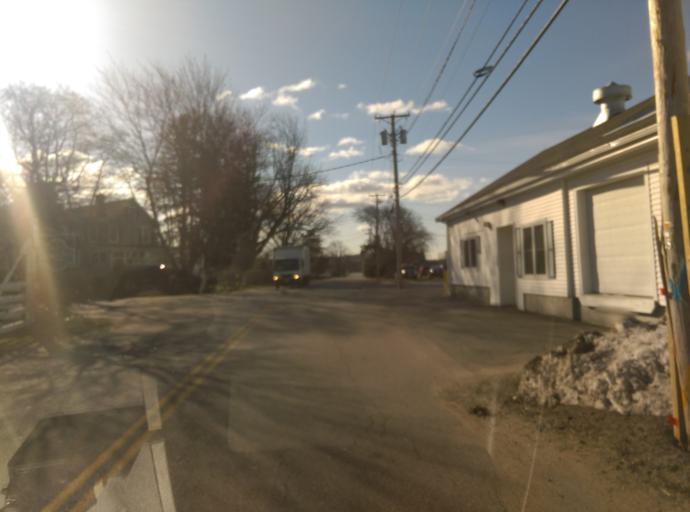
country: US
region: Massachusetts
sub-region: Essex County
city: Haverhill
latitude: 42.7537
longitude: -71.1172
